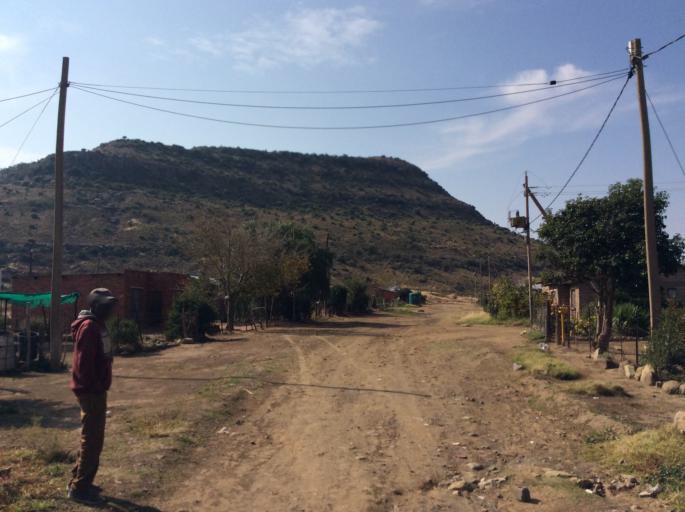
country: LS
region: Mafeteng
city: Mafeteng
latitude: -29.7186
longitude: 27.0343
